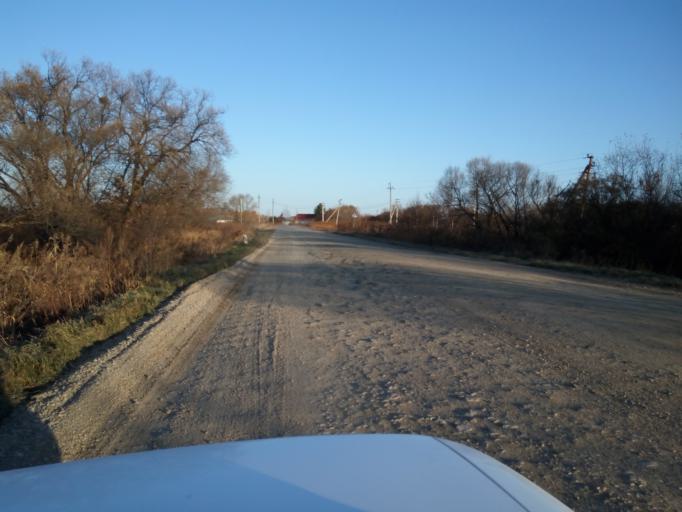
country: RU
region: Primorskiy
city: Lazo
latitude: 45.8566
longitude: 133.6465
